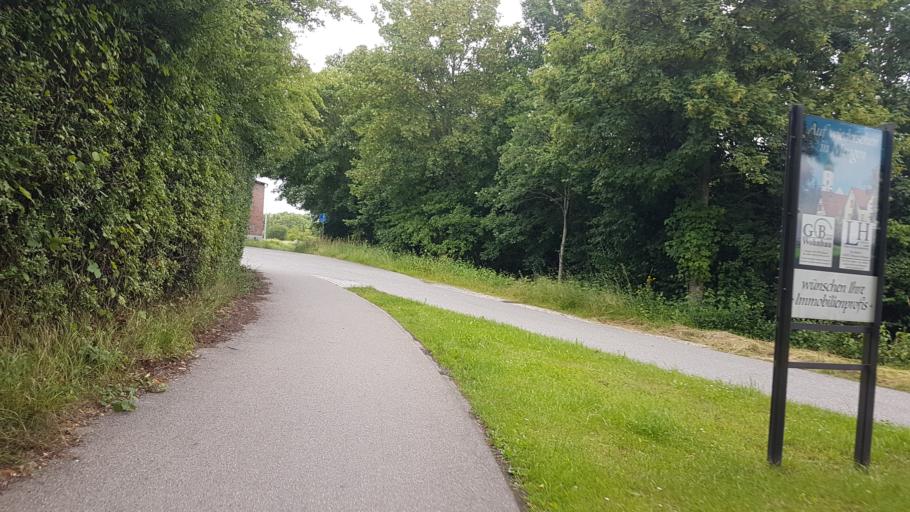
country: DE
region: Baden-Wuerttemberg
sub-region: Tuebingen Region
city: Mengen
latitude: 48.0528
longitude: 9.3402
